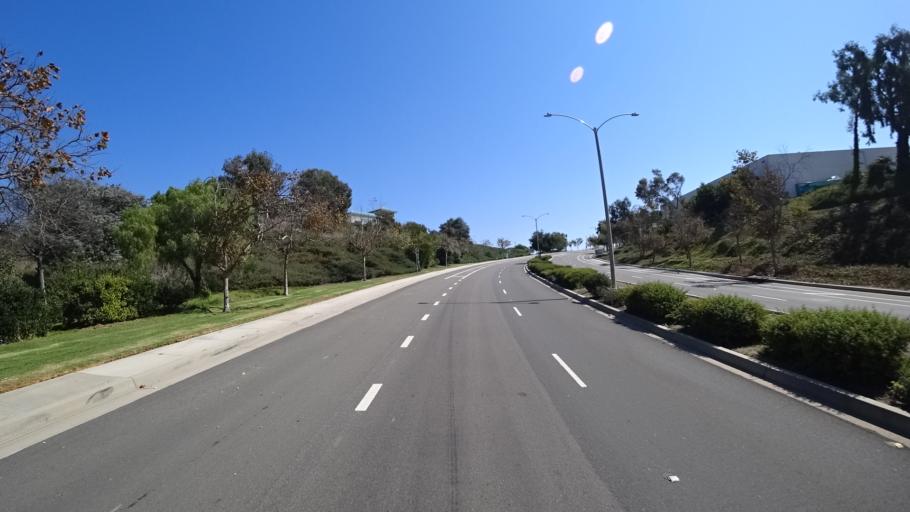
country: US
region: California
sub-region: Orange County
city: San Clemente
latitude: 33.4543
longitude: -117.5950
